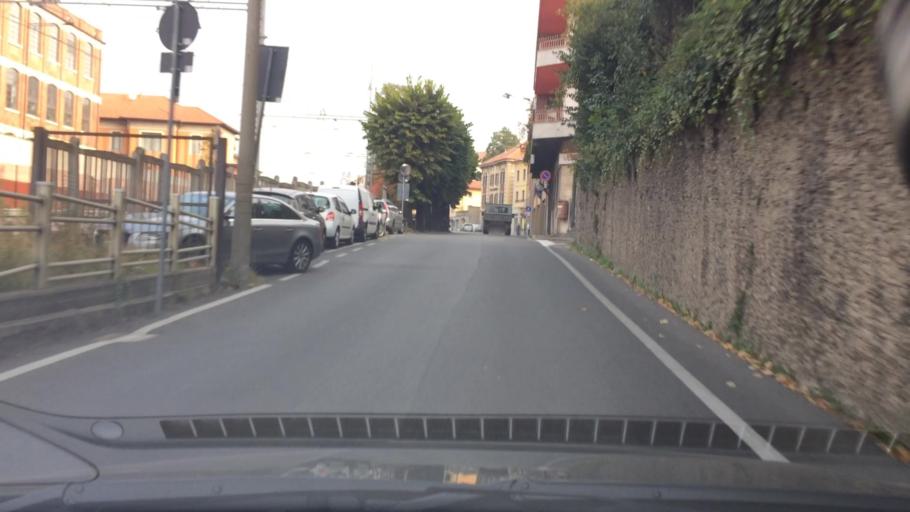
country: IT
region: Lombardy
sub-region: Provincia di Como
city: Lomazzo
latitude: 45.6973
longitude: 9.0362
